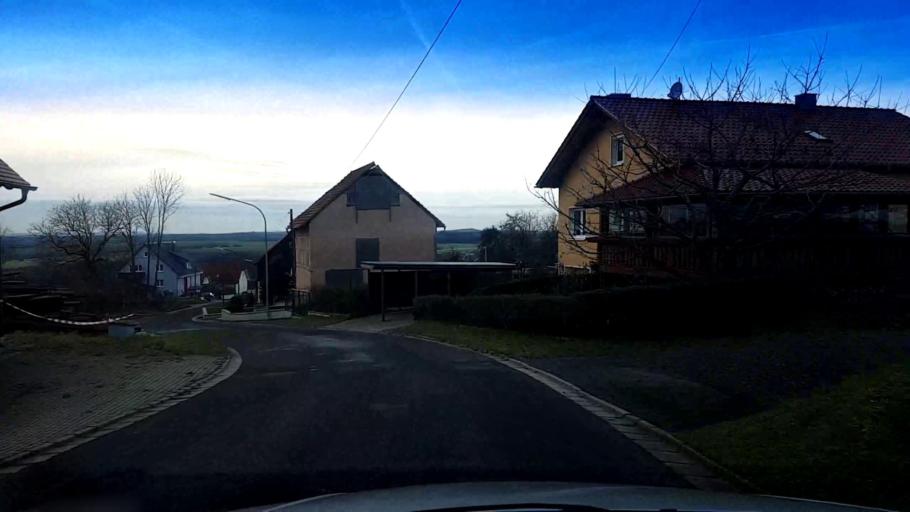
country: DE
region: Bavaria
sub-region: Upper Franconia
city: Schesslitz
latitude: 49.9866
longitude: 11.0589
